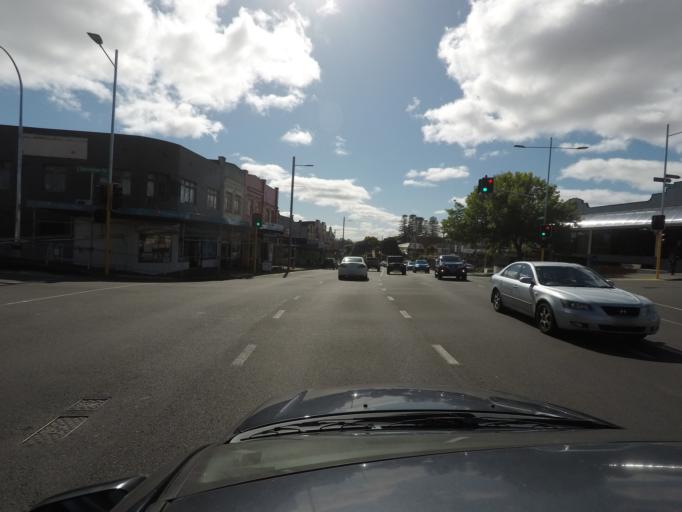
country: NZ
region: Auckland
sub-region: Auckland
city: Rosebank
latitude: -36.8841
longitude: 174.7154
